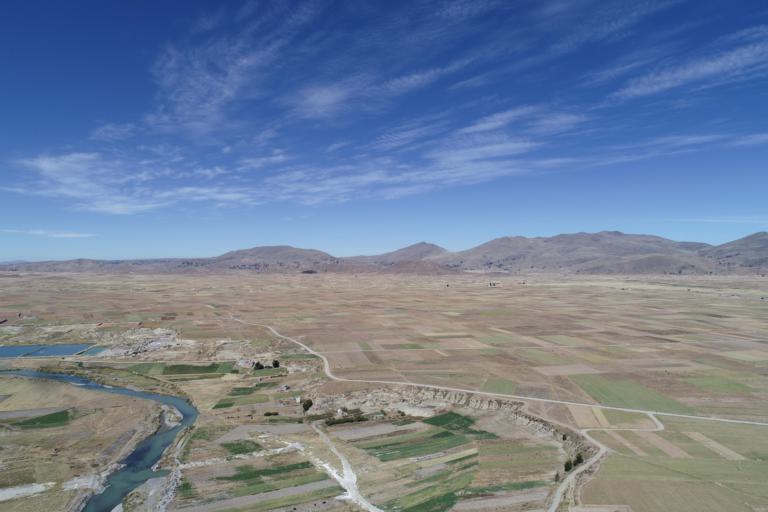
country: BO
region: La Paz
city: Achacachi
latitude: -16.0342
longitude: -68.7012
